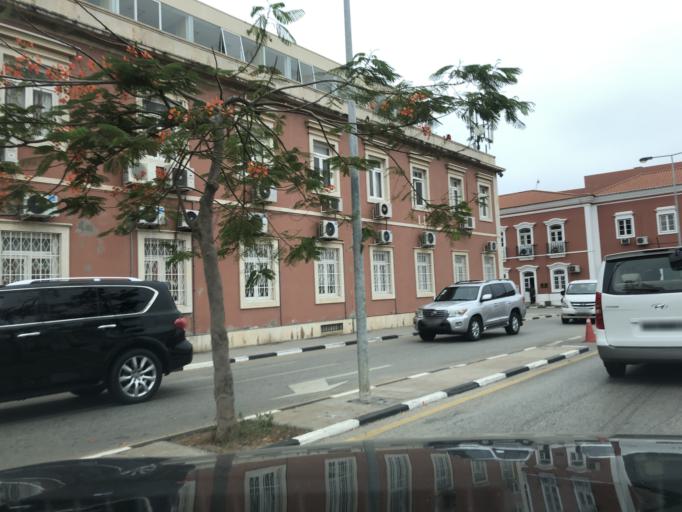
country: AO
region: Luanda
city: Luanda
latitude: -8.8185
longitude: 13.2250
